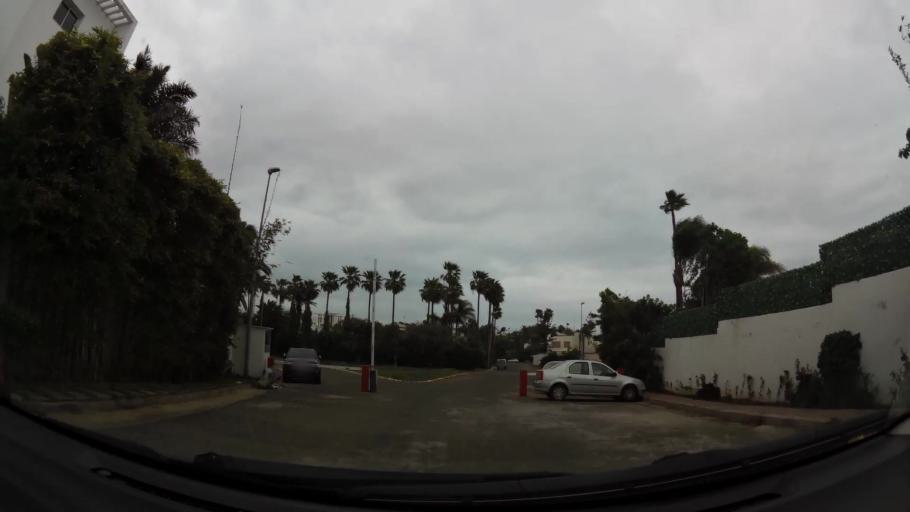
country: MA
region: Grand Casablanca
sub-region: Casablanca
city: Casablanca
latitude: 33.5956
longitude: -7.6614
